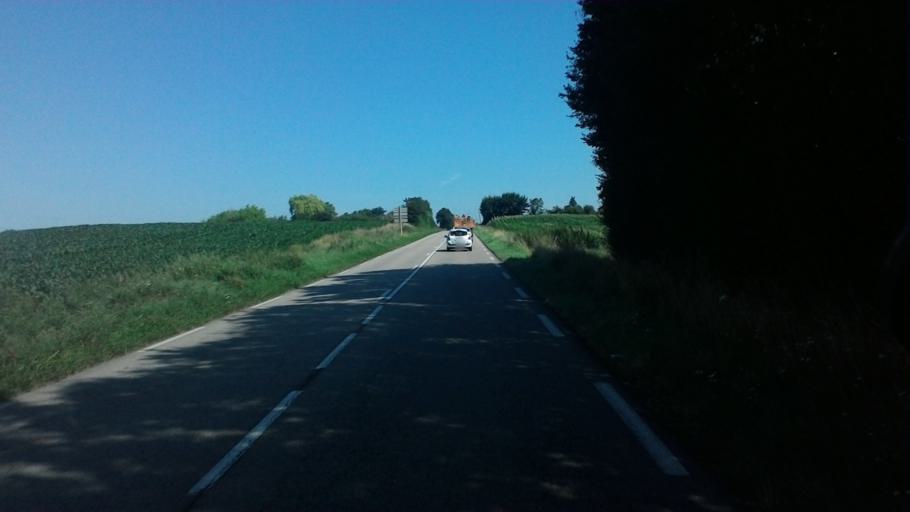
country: FR
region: Rhone-Alpes
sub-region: Departement de l'Ain
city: Saint-Trivier-de-Courtes
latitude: 46.4501
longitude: 5.0869
